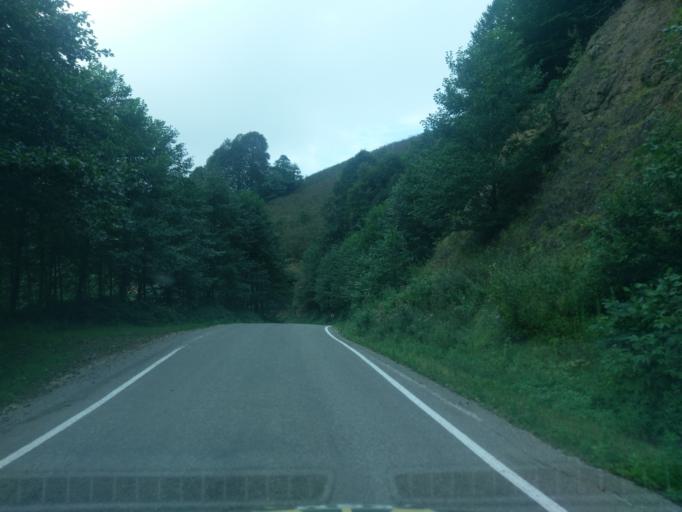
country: TR
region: Ordu
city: Gurgentepe
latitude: 40.8653
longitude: 37.6402
